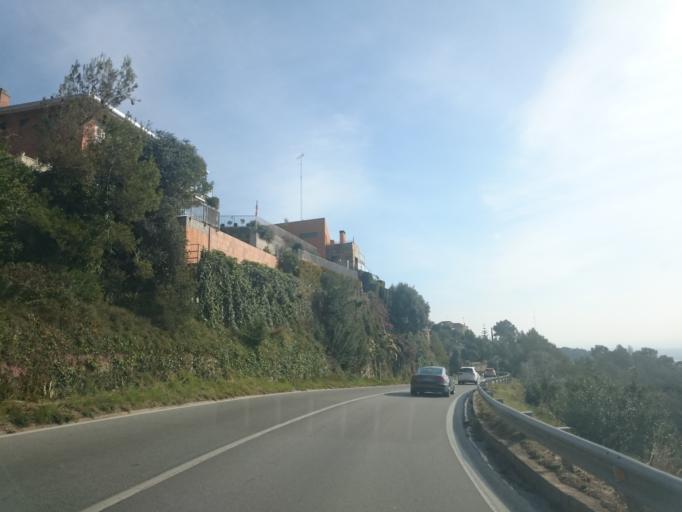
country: ES
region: Catalonia
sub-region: Provincia de Barcelona
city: Begues
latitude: 41.3148
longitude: 1.9634
